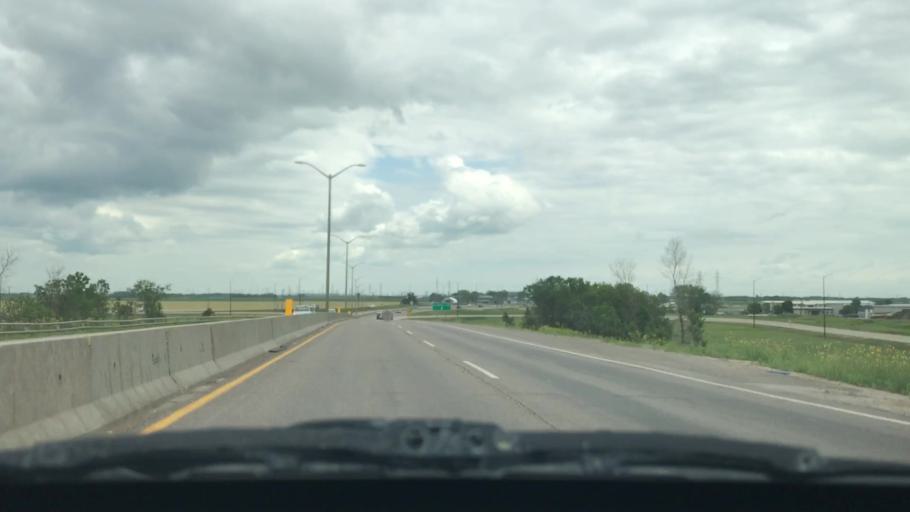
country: CA
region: Manitoba
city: Winnipeg
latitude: 49.8555
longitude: -97.0208
